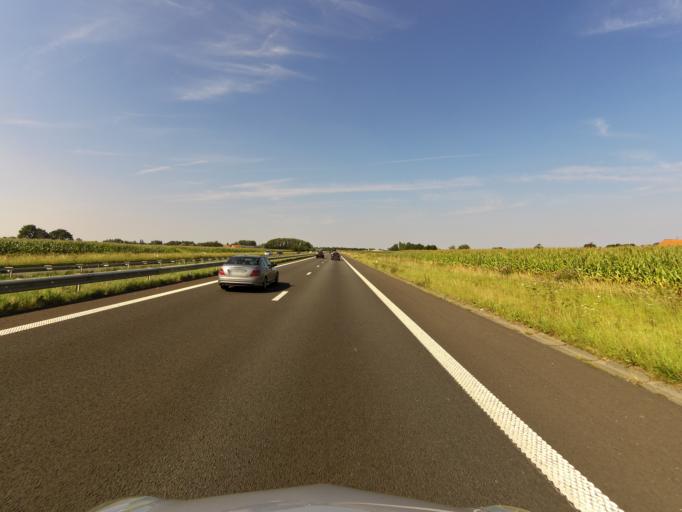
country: BE
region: Flanders
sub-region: Provincie West-Vlaanderen
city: Lichtervelde
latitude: 51.0482
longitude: 3.1615
